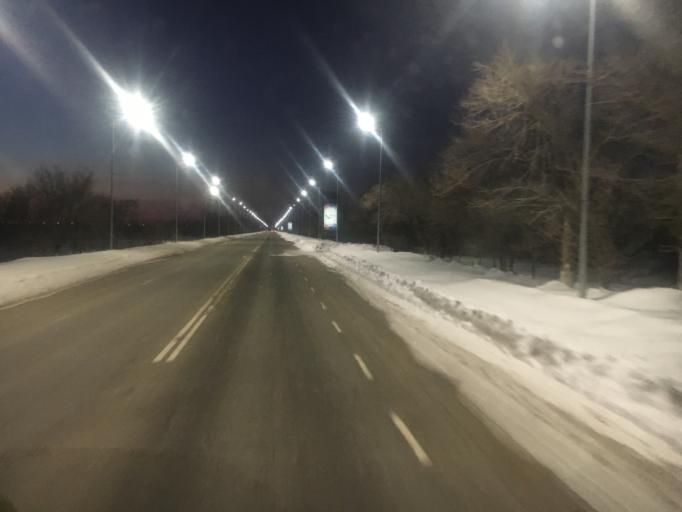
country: KZ
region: Batys Qazaqstan
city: Oral
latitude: 51.1549
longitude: 51.5370
